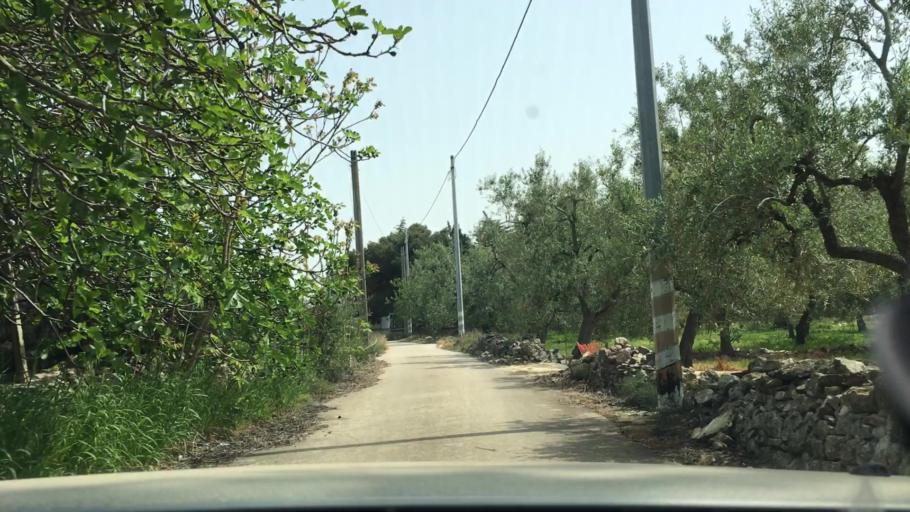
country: IT
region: Apulia
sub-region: Provincia di Barletta - Andria - Trani
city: Capirro
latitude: 41.2550
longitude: 16.4572
